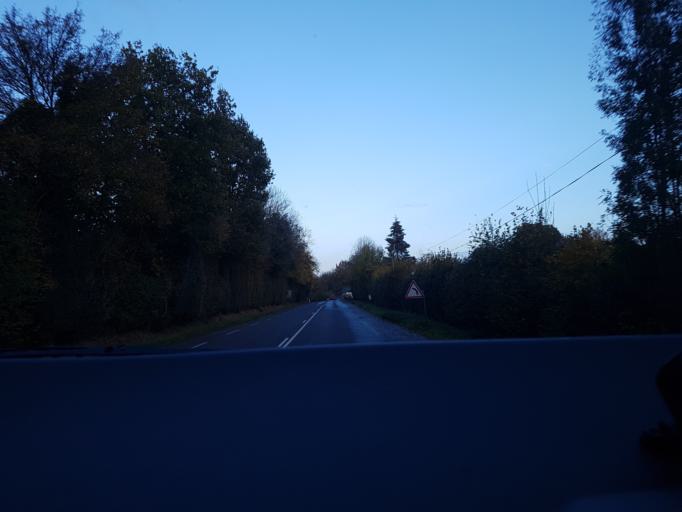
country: FR
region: Lower Normandy
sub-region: Departement du Calvados
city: Saint-Gatien-des-Bois
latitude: 49.2655
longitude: 0.1562
